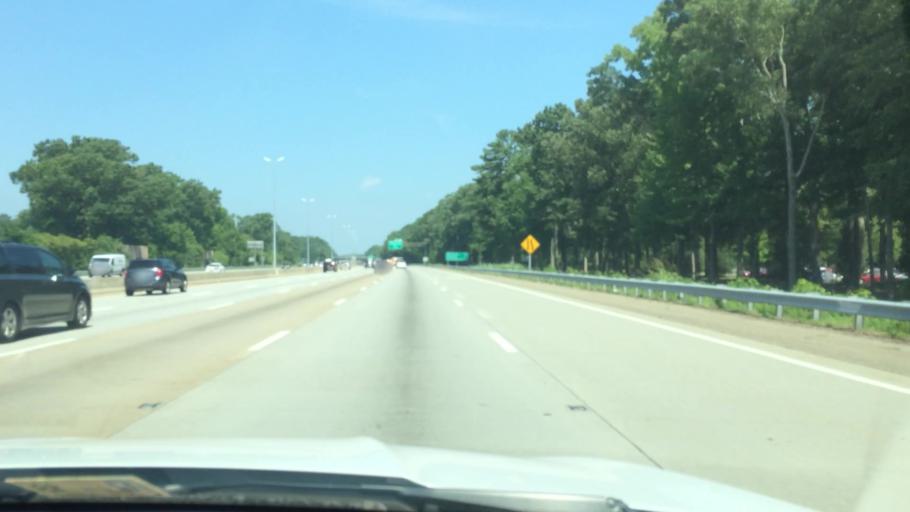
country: US
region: Virginia
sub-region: City of Hampton
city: Hampton
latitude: 37.0530
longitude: -76.4084
